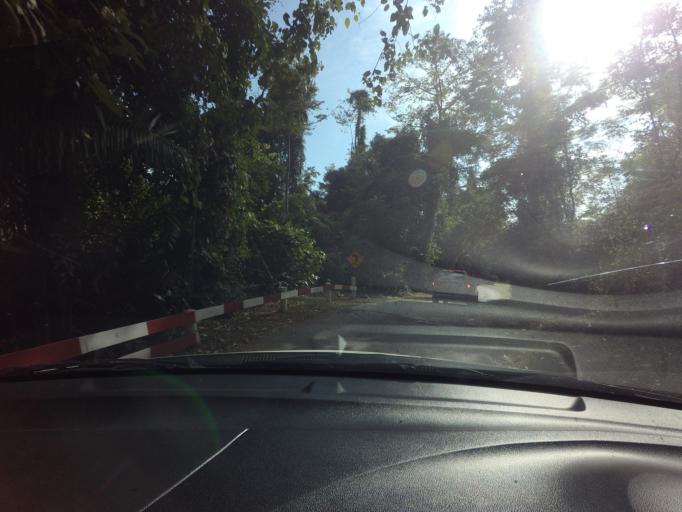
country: TH
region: Nakhon Nayok
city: Nakhon Nayok
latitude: 14.3282
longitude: 101.3068
